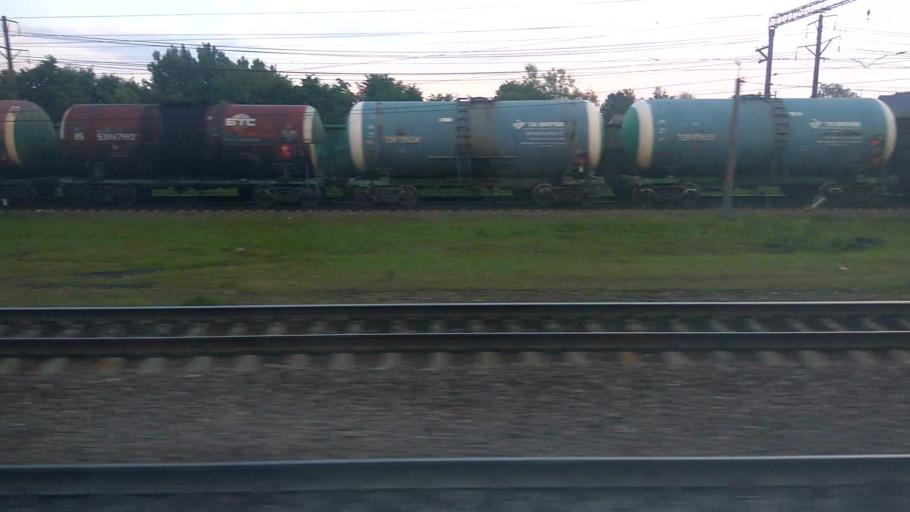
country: RU
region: Moskovskaya
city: Mikhnevo
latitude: 55.1239
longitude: 37.9601
